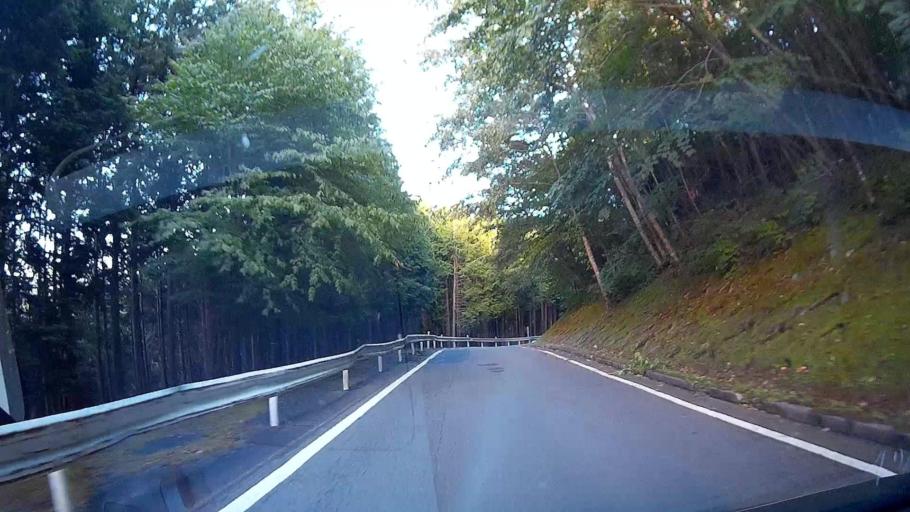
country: JP
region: Shizuoka
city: Shizuoka-shi
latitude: 35.1729
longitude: 138.2550
